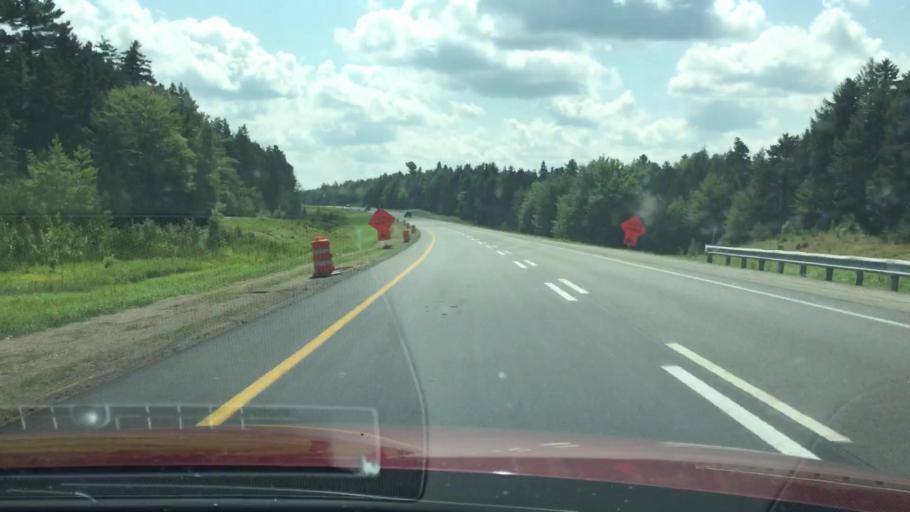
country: US
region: Maine
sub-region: Penobscot County
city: Medway
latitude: 45.6741
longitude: -68.4985
